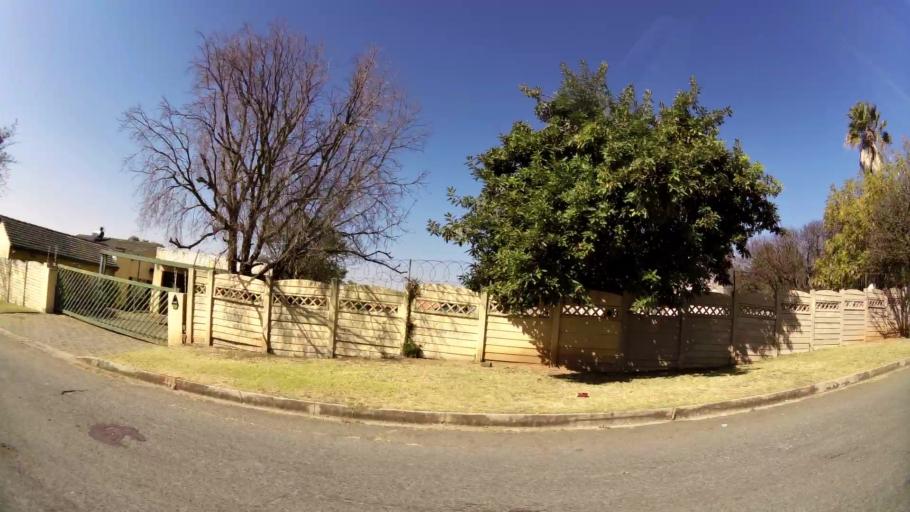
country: ZA
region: Gauteng
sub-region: City of Johannesburg Metropolitan Municipality
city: Modderfontein
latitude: -26.0573
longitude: 28.2098
